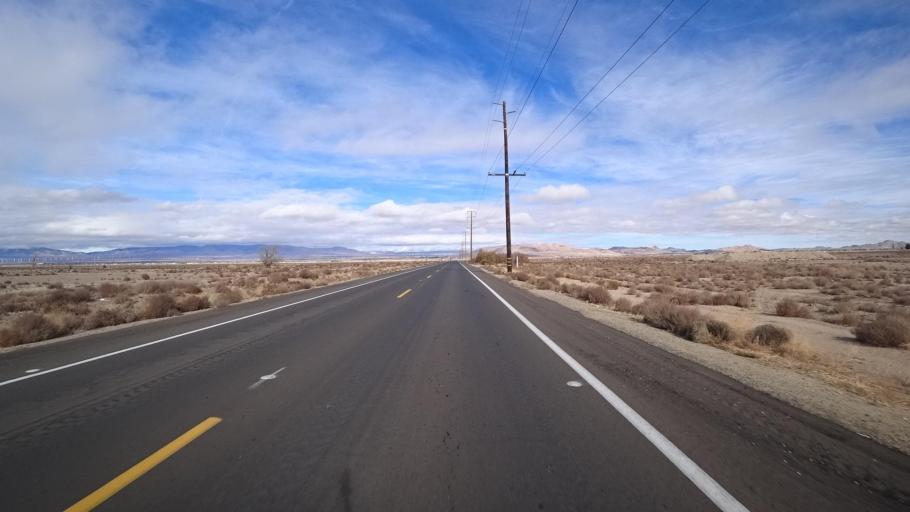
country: US
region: California
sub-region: Kern County
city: Rosamond
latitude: 34.8264
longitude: -118.2906
